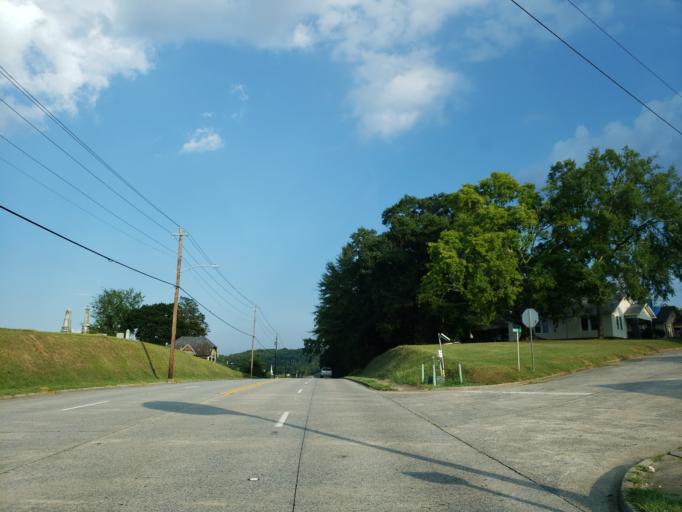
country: US
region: Georgia
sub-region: Polk County
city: Rockmart
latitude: 34.0016
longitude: -85.0565
